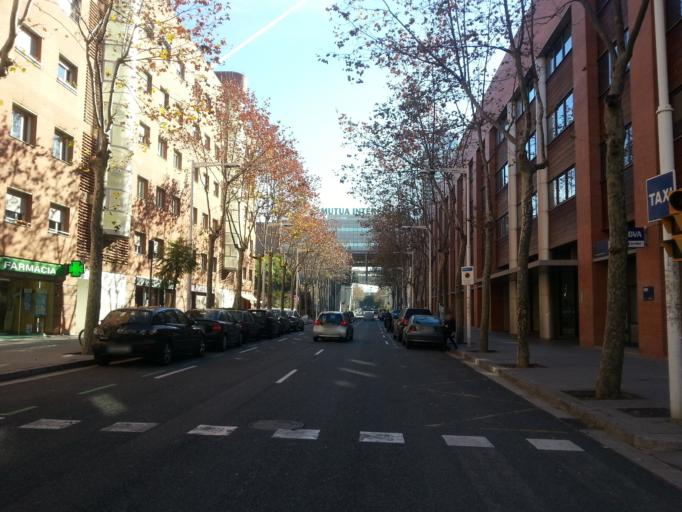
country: ES
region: Catalonia
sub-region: Provincia de Barcelona
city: Ciutat Vella
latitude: 41.3912
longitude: 2.1939
